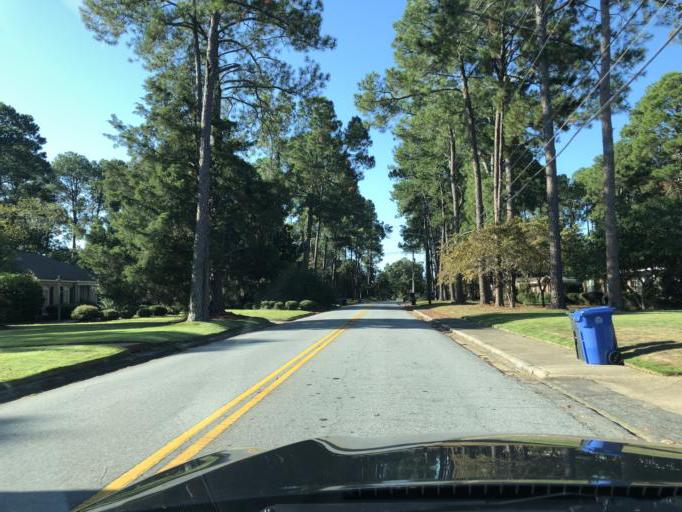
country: US
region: Georgia
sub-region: Muscogee County
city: Columbus
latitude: 32.4870
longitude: -84.9456
